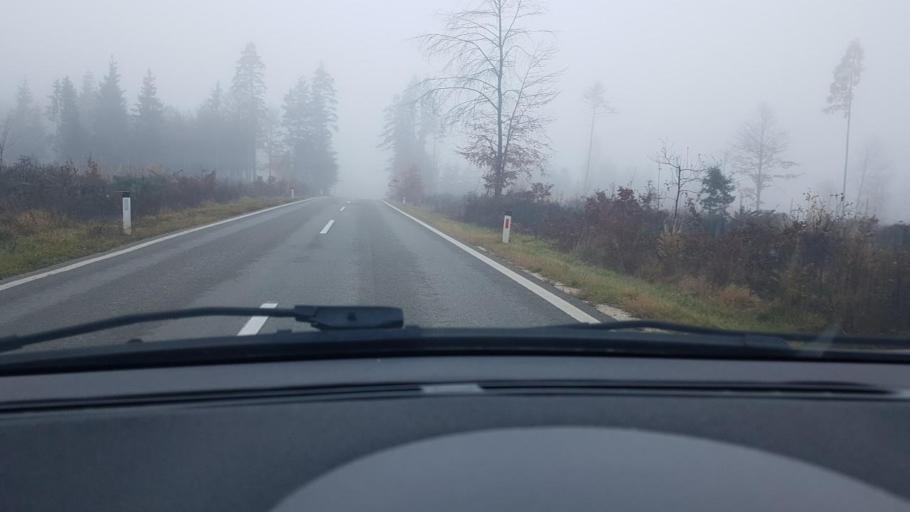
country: AT
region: Carinthia
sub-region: Politischer Bezirk Volkermarkt
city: Sittersdorf
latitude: 46.5479
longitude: 14.6202
